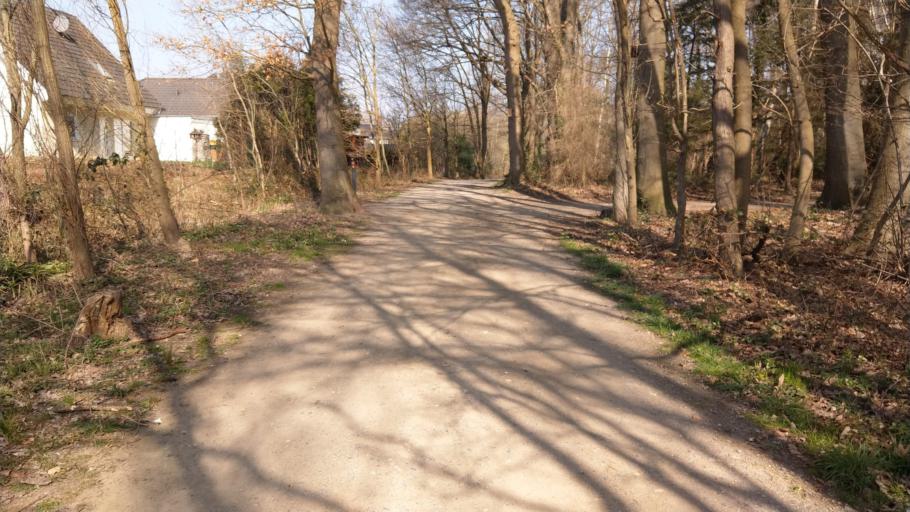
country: DE
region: North Rhine-Westphalia
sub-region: Regierungsbezirk Koln
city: Wassenberg
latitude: 51.1049
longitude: 6.1596
